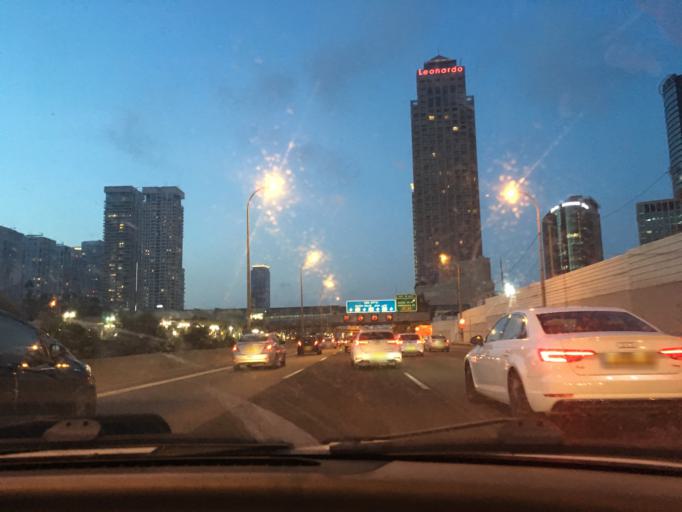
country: IL
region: Tel Aviv
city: Ramat Gan
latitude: 32.0822
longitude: 34.7983
